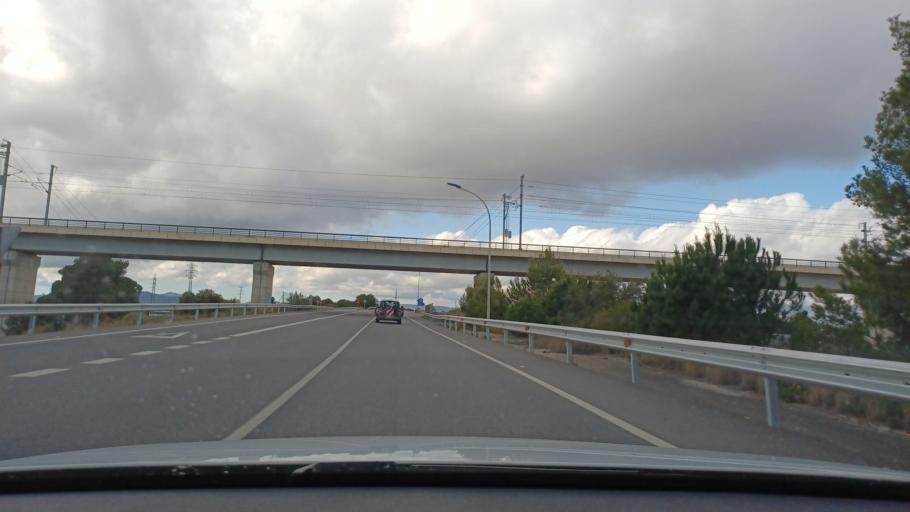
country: ES
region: Catalonia
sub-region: Provincia de Tarragona
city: Cambrils
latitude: 41.0792
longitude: 1.0418
